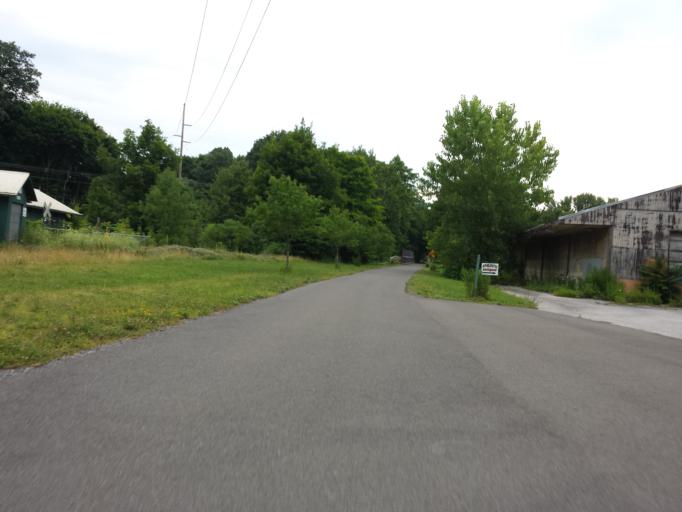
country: US
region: New York
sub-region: Ulster County
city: Highland
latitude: 41.7161
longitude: -73.9679
